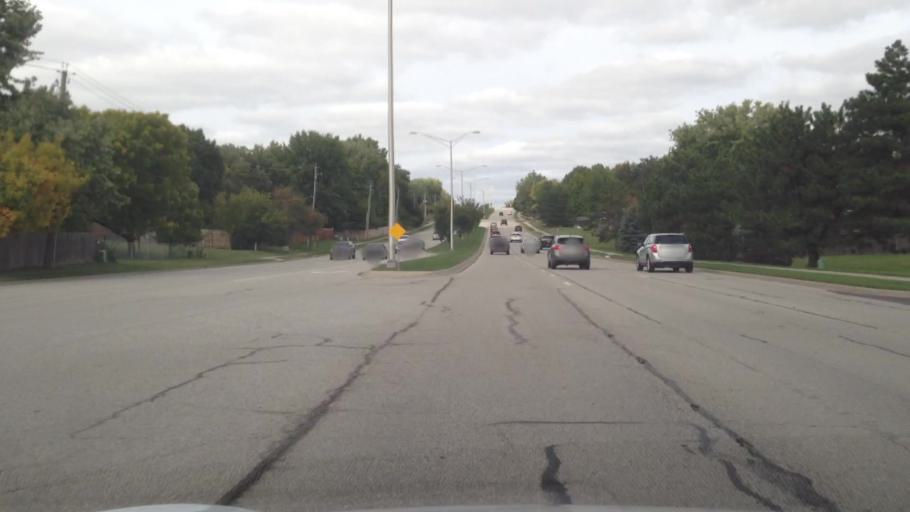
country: US
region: Kansas
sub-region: Johnson County
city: Lenexa
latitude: 38.9154
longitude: -94.7236
